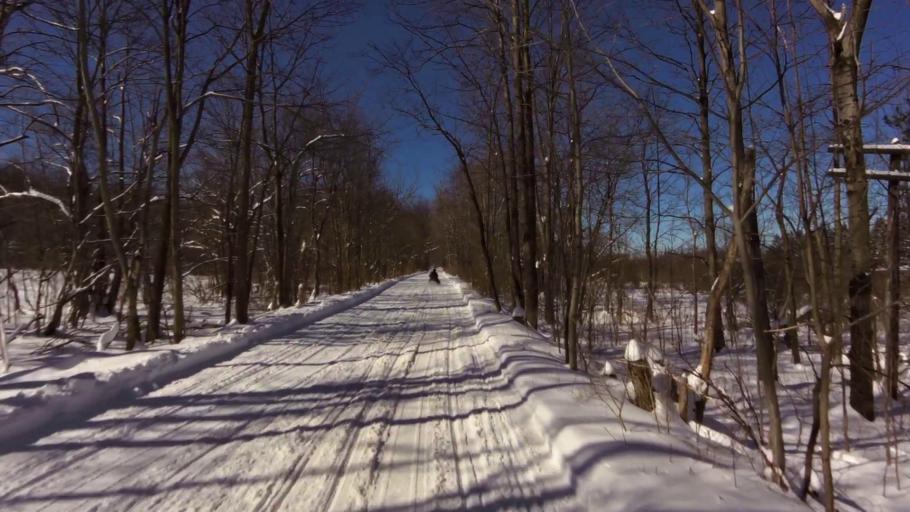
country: US
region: New York
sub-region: Chautauqua County
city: Mayville
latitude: 42.2371
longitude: -79.5129
